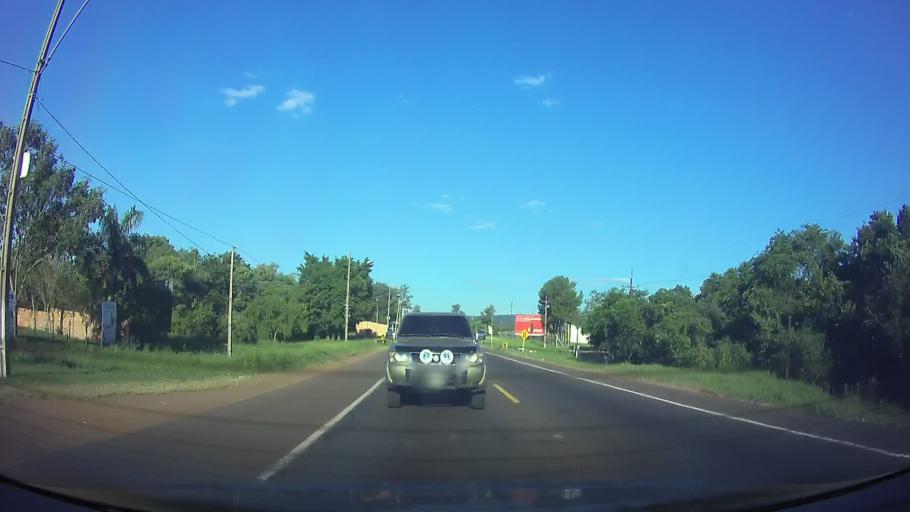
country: PY
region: Central
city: Ypacarai
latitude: -25.3810
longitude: -57.2509
